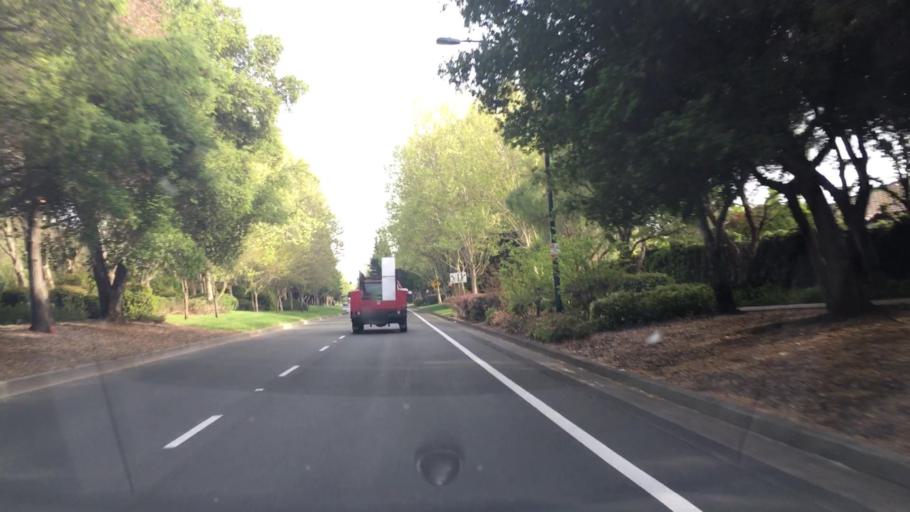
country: US
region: California
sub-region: Solano County
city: Green Valley
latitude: 38.2244
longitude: -122.1460
